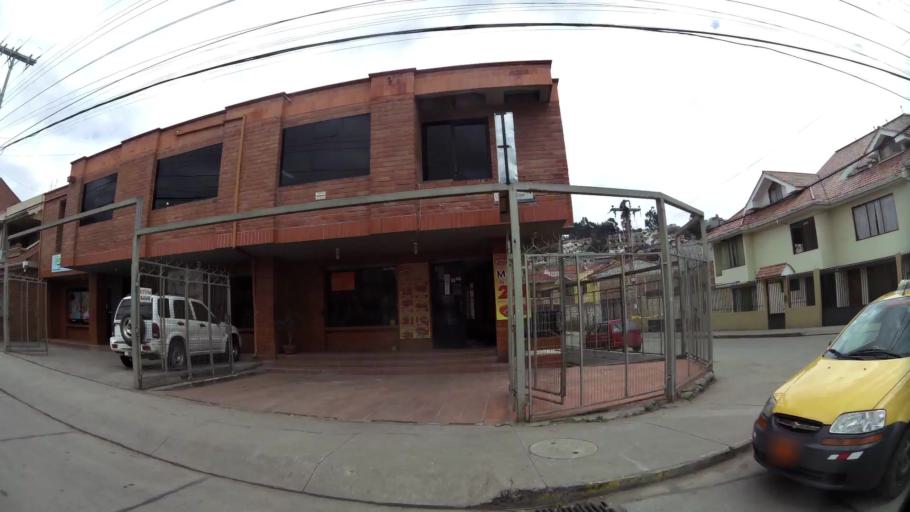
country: EC
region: Azuay
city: Cuenca
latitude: -2.8879
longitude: -79.0300
